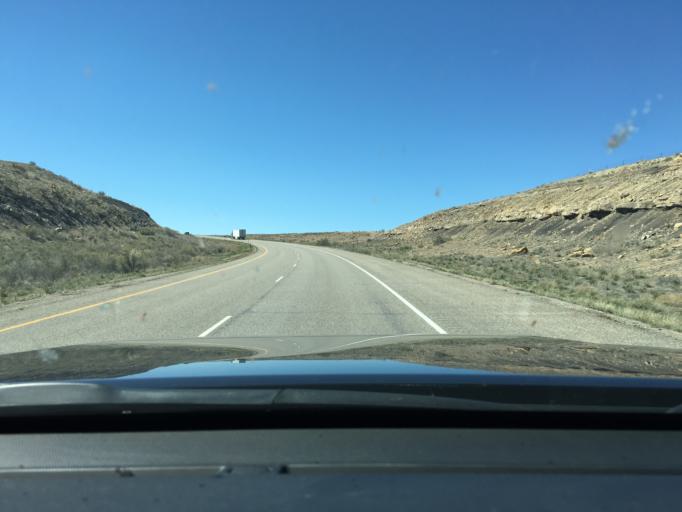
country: US
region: Colorado
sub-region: Mesa County
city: Loma
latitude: 39.2325
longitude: -108.9050
